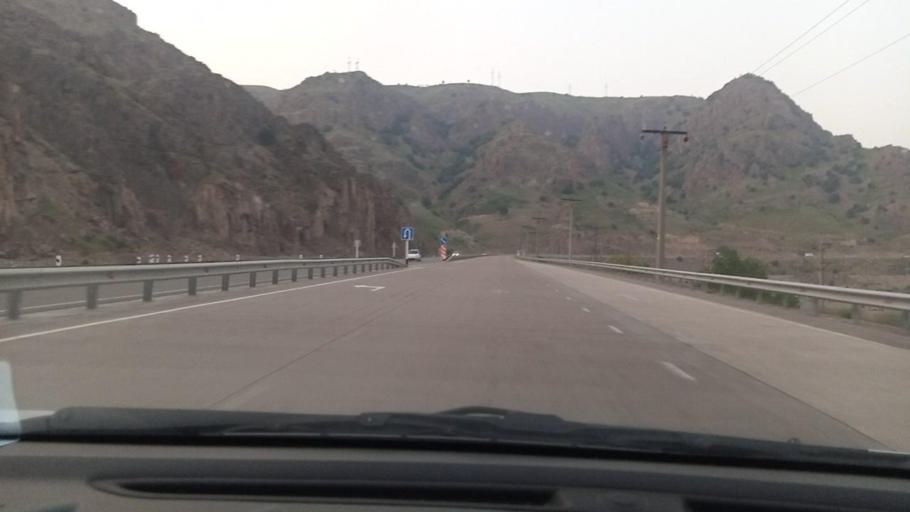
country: UZ
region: Toshkent
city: Angren
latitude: 41.1323
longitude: 70.3719
